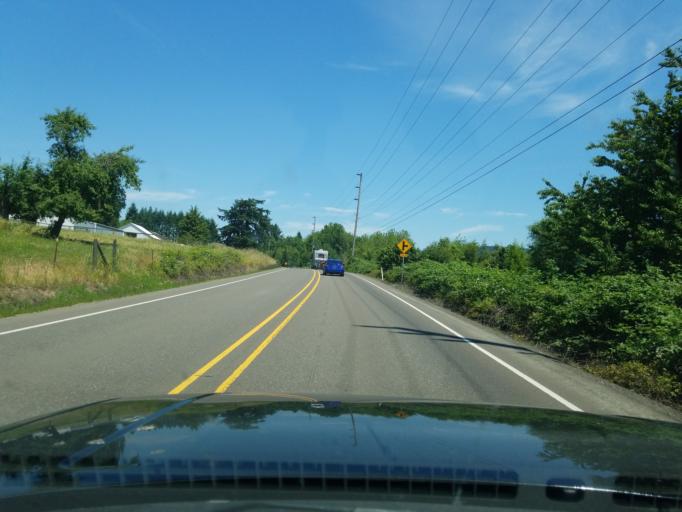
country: US
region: Oregon
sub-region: Yamhill County
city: Yamhill
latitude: 45.4021
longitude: -123.1242
